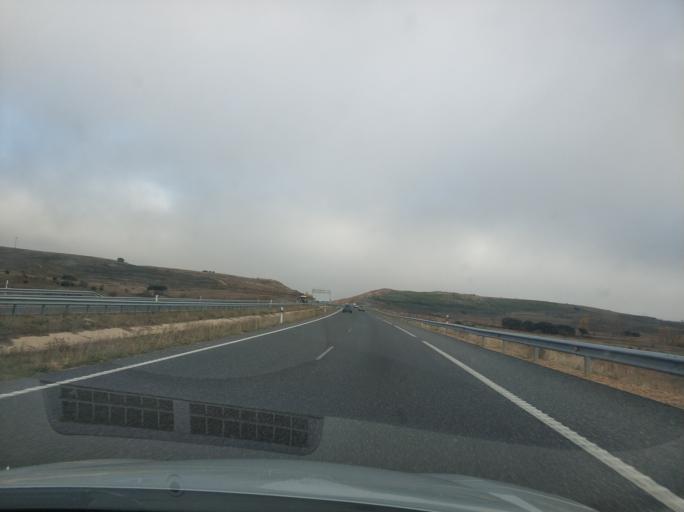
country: ES
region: Castille and Leon
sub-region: Provincia de Leon
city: Leon
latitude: 42.5644
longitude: -5.5395
